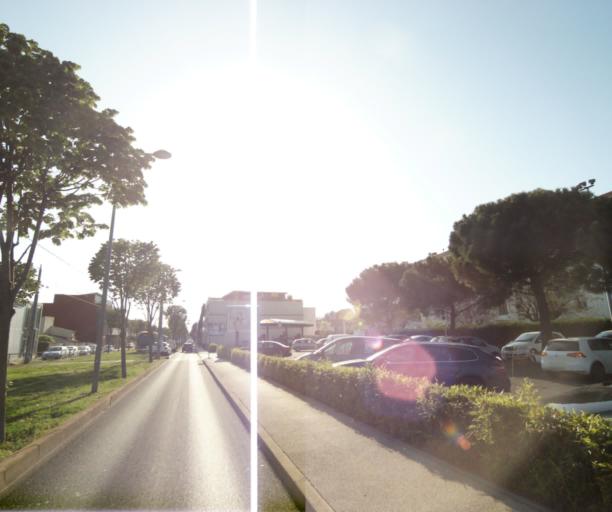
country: FR
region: Languedoc-Roussillon
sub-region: Departement de l'Herault
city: Castelnau-le-Lez
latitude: 43.6312
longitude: 3.9072
